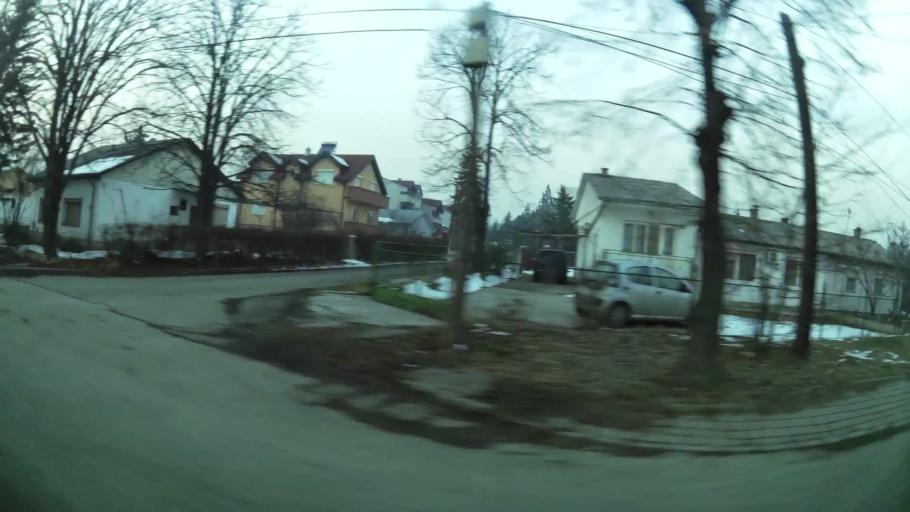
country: MK
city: Creshevo
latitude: 42.0054
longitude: 21.5093
